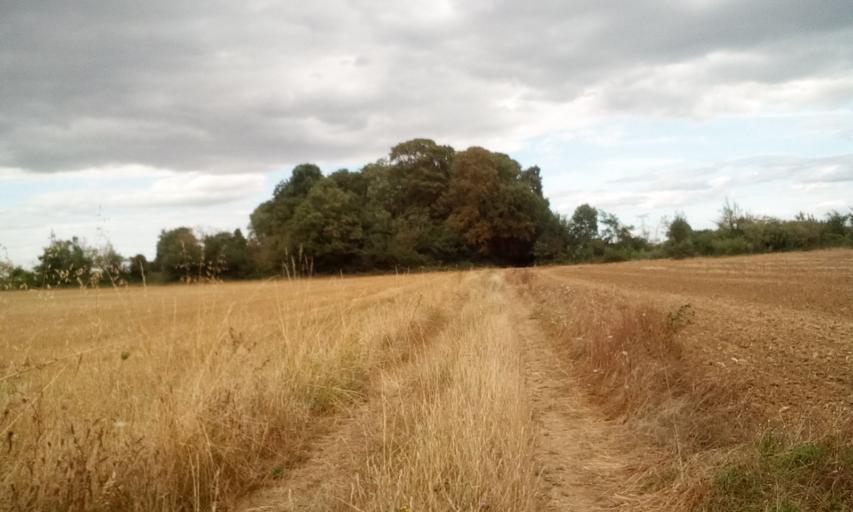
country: FR
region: Lower Normandy
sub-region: Departement du Calvados
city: Bellengreville
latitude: 49.1263
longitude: -0.2228
